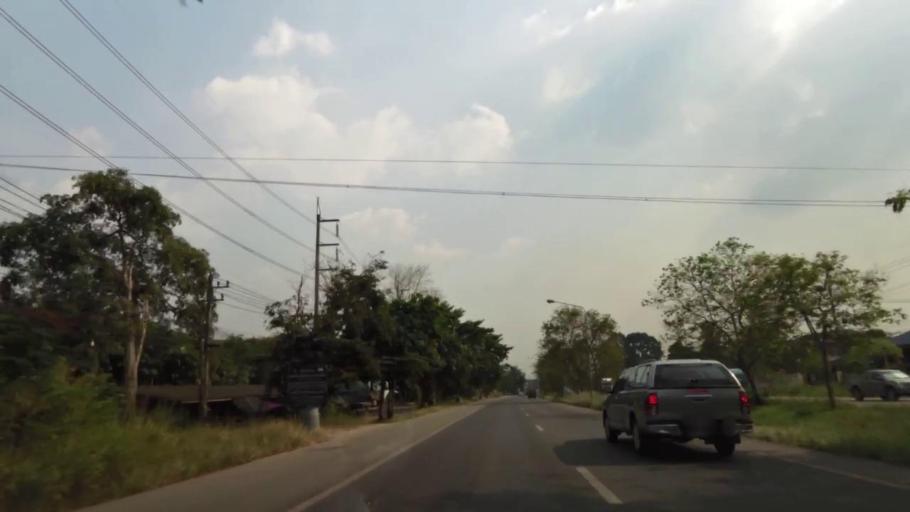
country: TH
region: Rayong
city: Klaeng
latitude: 12.8448
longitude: 101.6213
